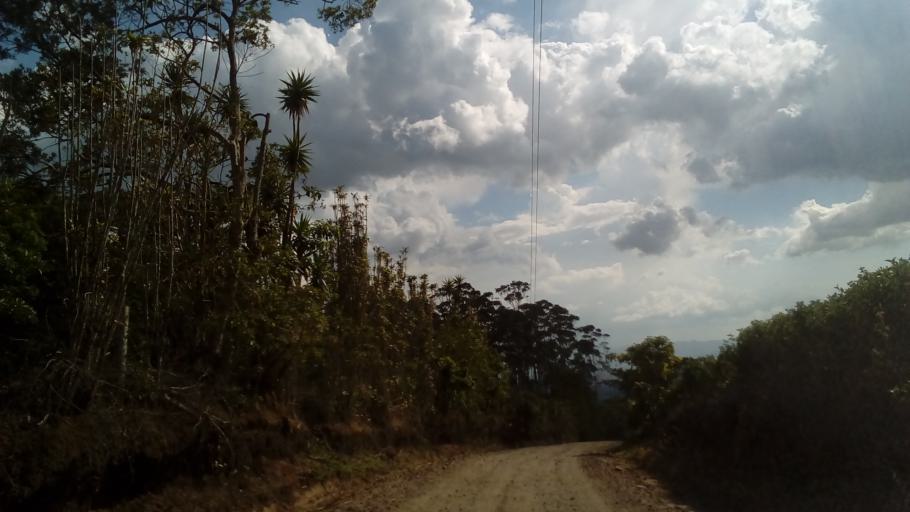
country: CR
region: Alajuela
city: San Juan
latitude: 10.1354
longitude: -84.2534
